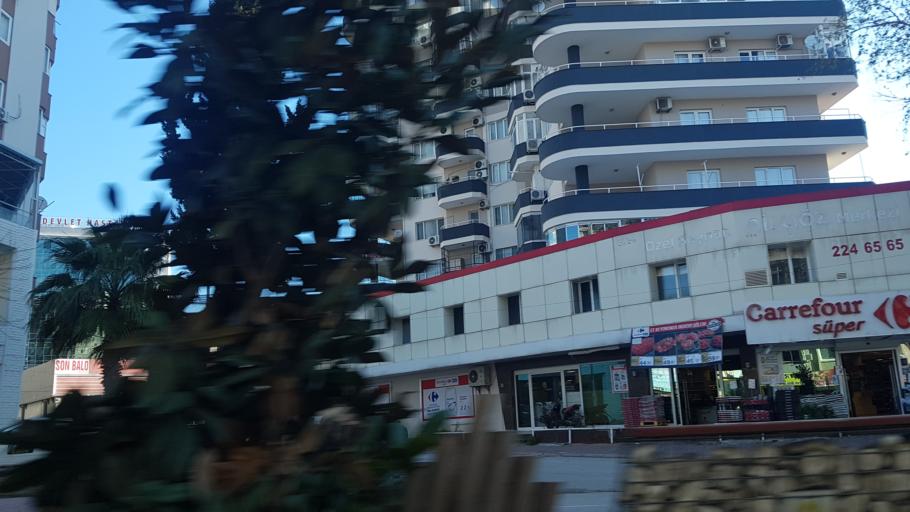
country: TR
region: Adana
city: Adana
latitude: 37.0175
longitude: 35.3181
